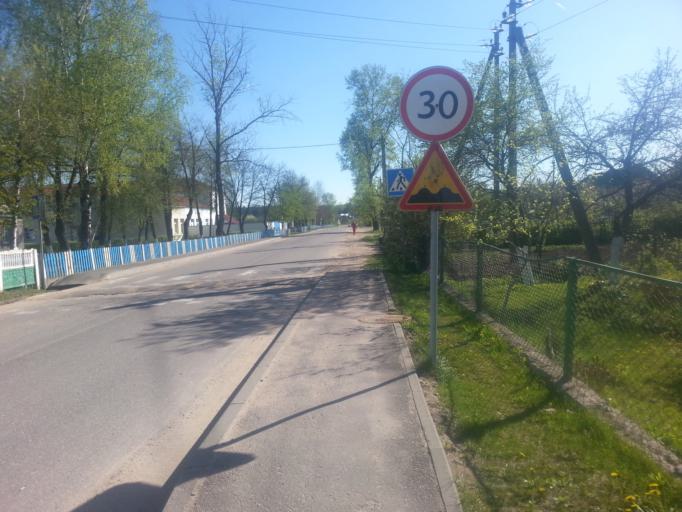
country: BY
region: Minsk
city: Narach
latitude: 54.9314
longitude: 26.6855
